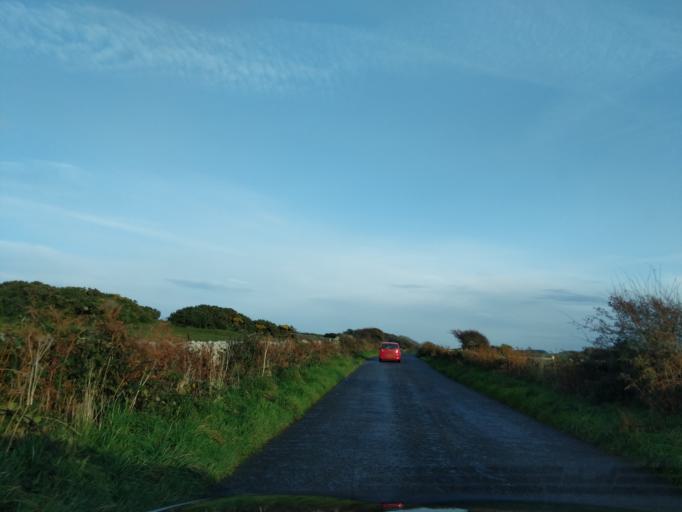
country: GB
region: Scotland
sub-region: Dumfries and Galloway
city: Kirkcudbright
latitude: 54.8112
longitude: -4.1912
